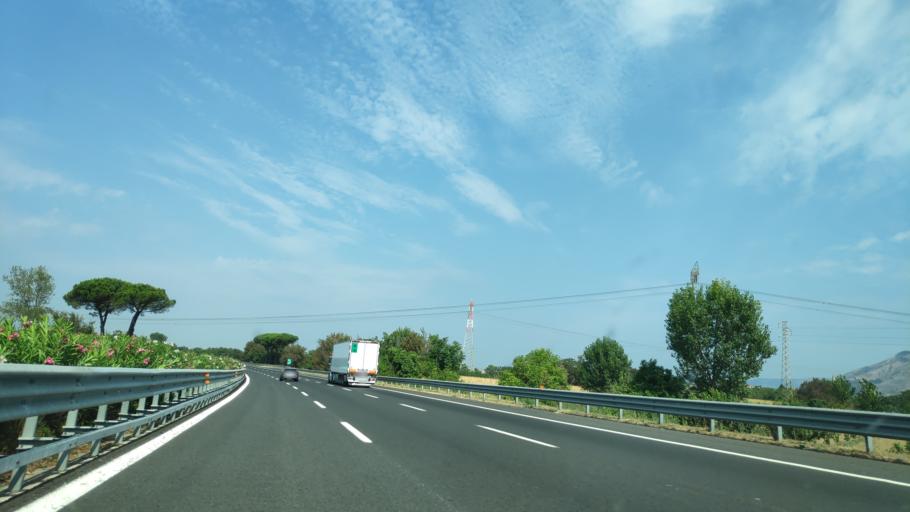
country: IT
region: Campania
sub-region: Provincia di Caserta
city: Montedecoro
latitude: 41.0090
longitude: 14.3983
